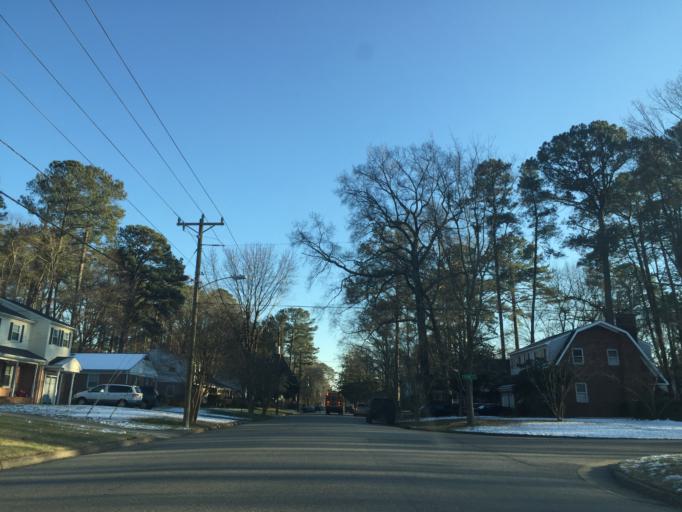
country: US
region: Virginia
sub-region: City of Newport News
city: Newport News
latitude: 37.0794
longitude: -76.4878
